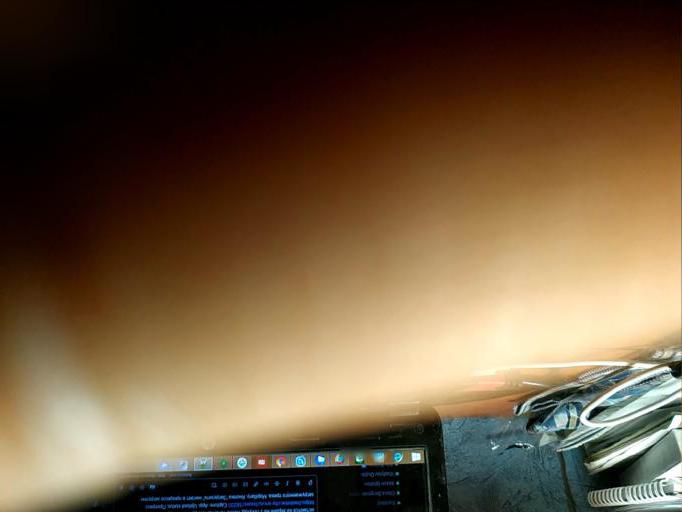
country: RU
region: Tverskaya
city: Likhoslavl'
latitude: 57.3081
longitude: 35.6880
